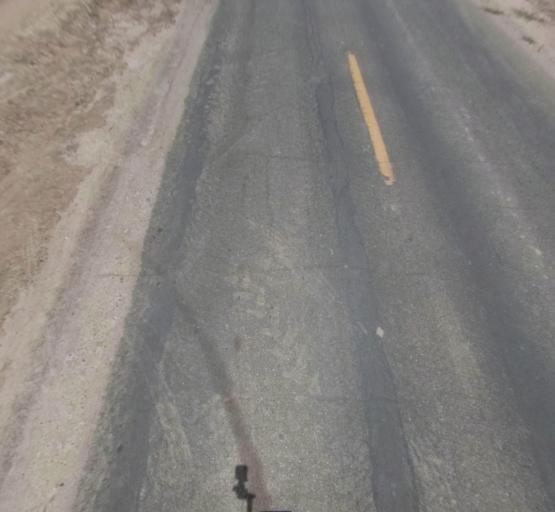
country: US
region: California
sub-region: Madera County
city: Parkwood
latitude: 36.8747
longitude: -120.0922
